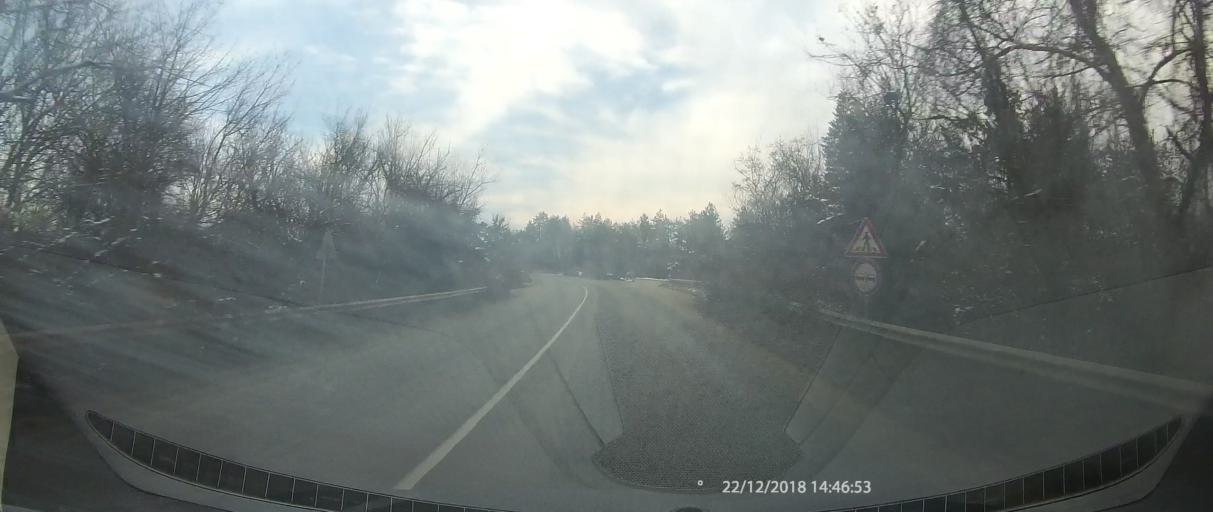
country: BG
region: Veliko Turnovo
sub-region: Obshtina Pavlikeni
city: Pavlikeni
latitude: 43.4141
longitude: 25.3716
